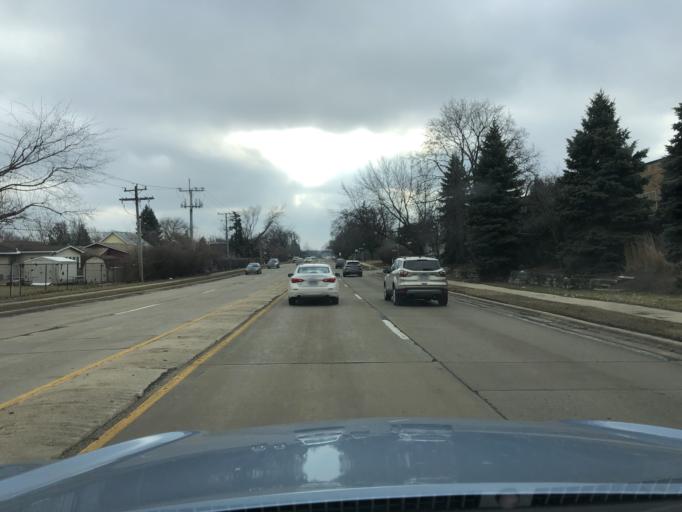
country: US
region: Illinois
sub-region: DuPage County
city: Itasca
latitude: 41.9998
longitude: -88.0036
